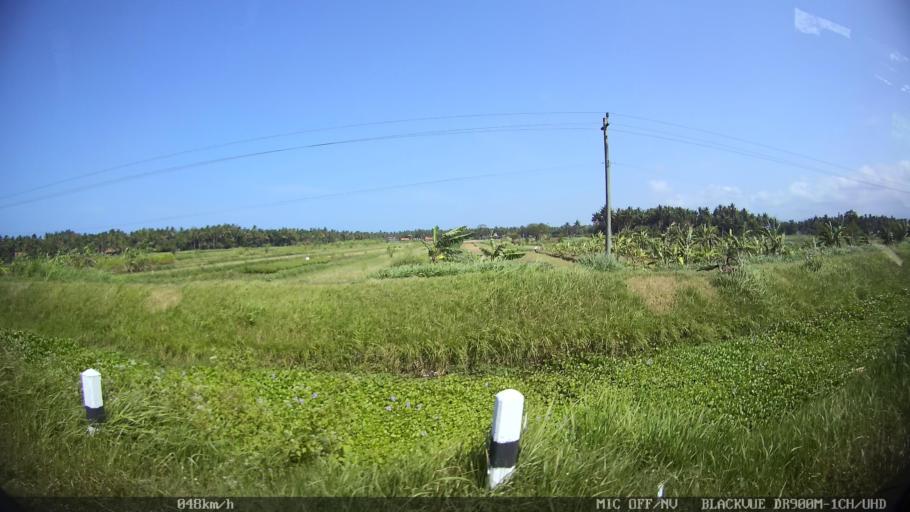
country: ID
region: Daerah Istimewa Yogyakarta
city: Srandakan
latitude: -7.9343
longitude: 110.1550
